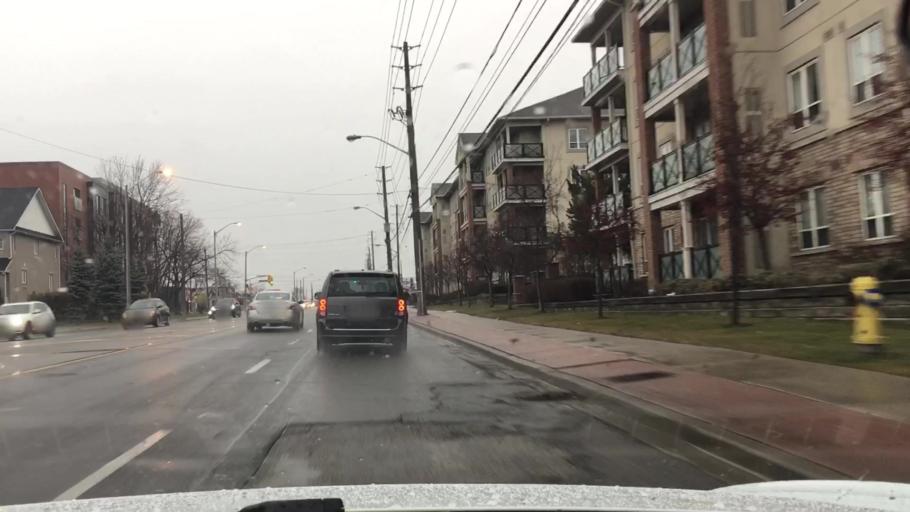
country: CA
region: Ontario
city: Scarborough
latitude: 43.7166
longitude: -79.2829
